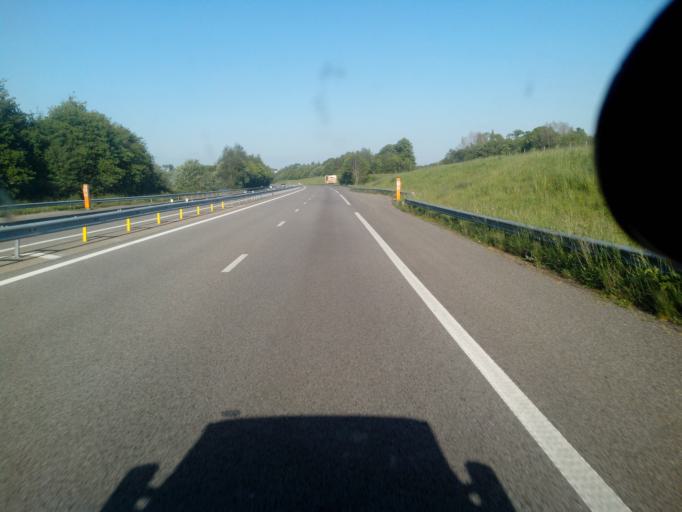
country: FR
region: Haute-Normandie
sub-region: Departement de la Seine-Maritime
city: La Remuee
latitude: 49.5695
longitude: 0.3871
